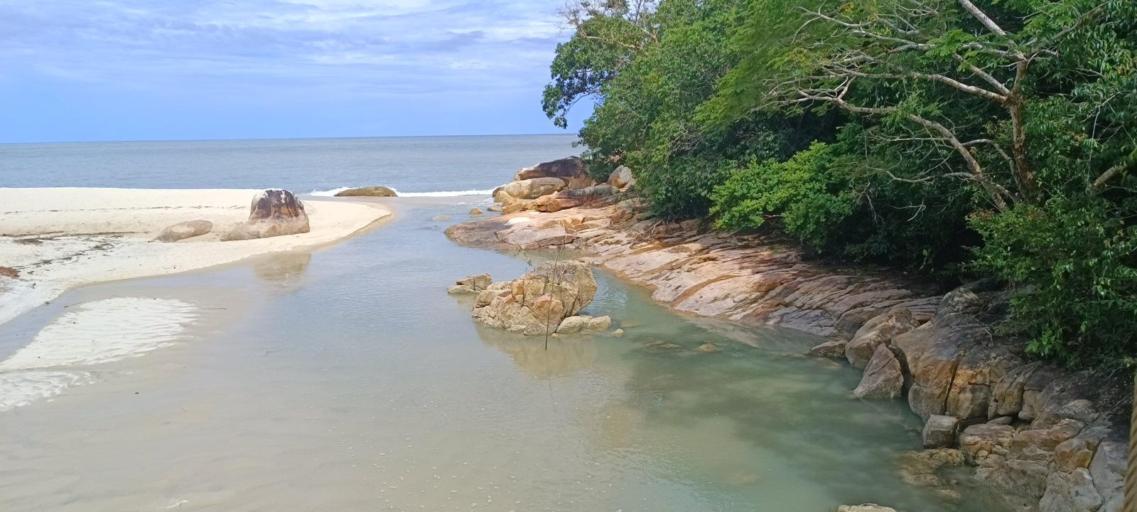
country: MY
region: Penang
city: Tanjung Tokong
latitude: 5.4532
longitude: 100.1844
